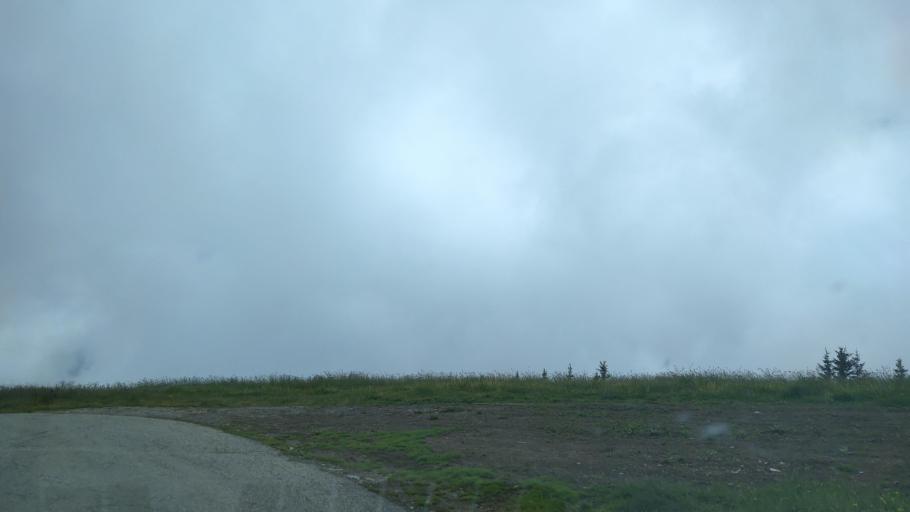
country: FR
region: Rhone-Alpes
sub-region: Departement de la Savoie
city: Beaufort
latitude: 45.7484
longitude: 6.5121
